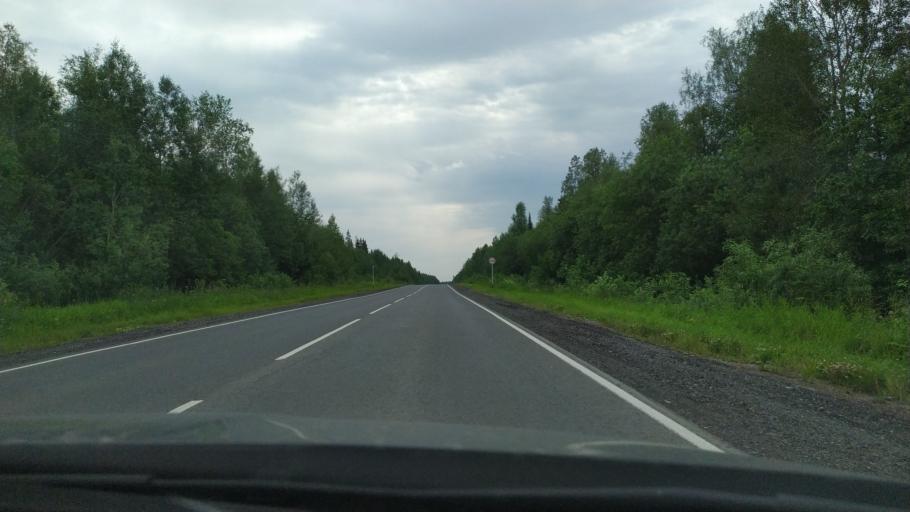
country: RU
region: Perm
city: Chusovoy
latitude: 58.4037
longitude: 57.8804
